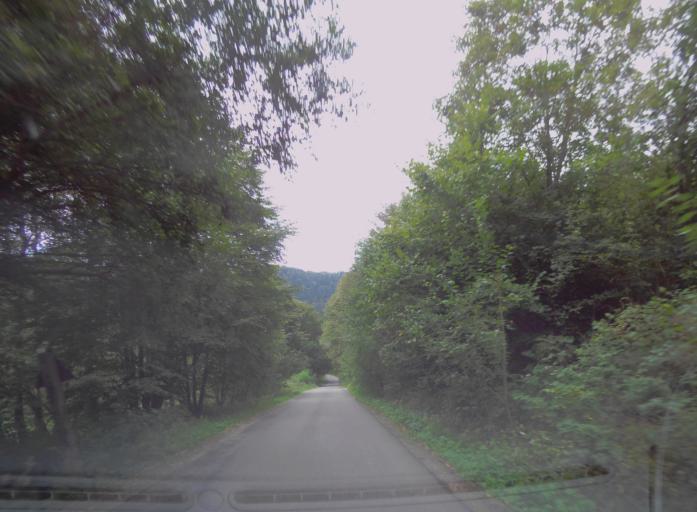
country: PL
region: Subcarpathian Voivodeship
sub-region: Powiat leski
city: Polanczyk
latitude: 49.2959
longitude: 22.5074
